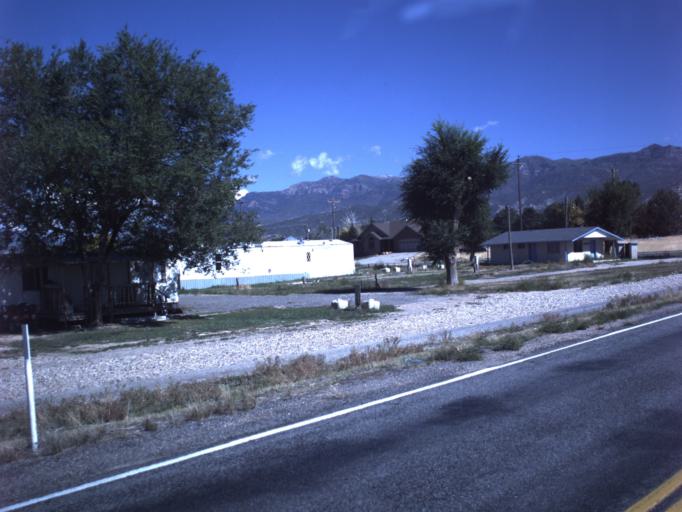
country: US
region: Utah
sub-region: Juab County
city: Nephi
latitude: 39.5587
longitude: -111.8689
